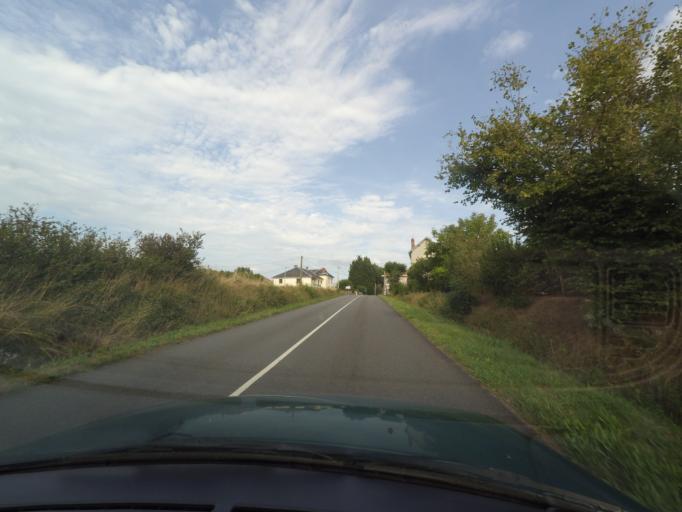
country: FR
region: Limousin
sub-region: Departement de la Haute-Vienne
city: Sereilhac
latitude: 45.7739
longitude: 1.0299
